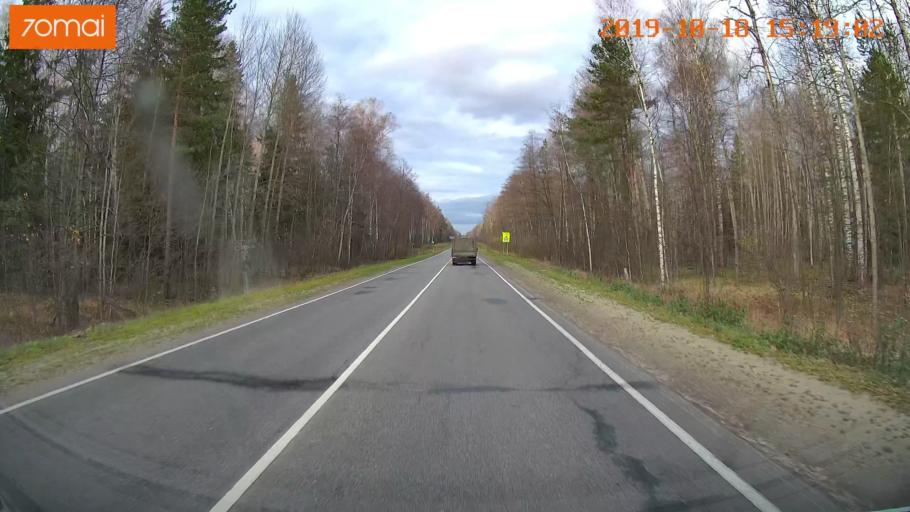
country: RU
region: Vladimir
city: Anopino
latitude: 55.6672
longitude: 40.7347
